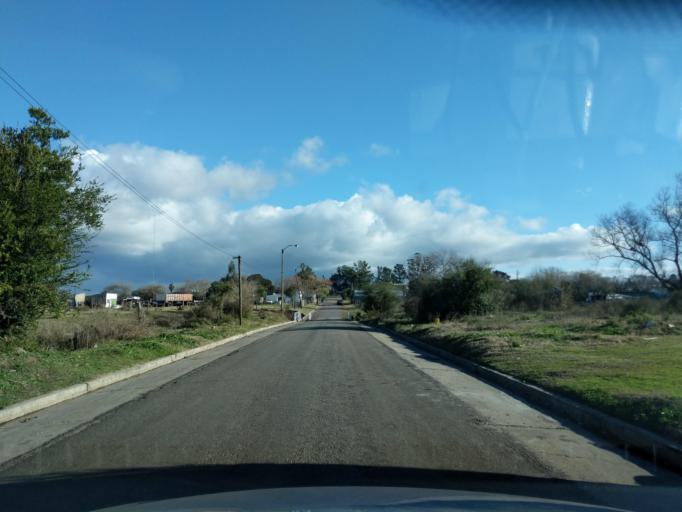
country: UY
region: Florida
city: Florida
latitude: -34.1066
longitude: -56.2203
